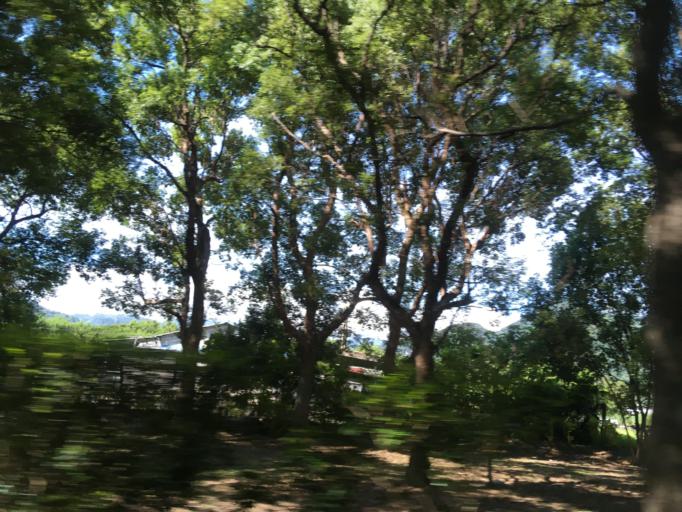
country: TW
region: Taiwan
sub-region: Yilan
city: Yilan
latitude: 24.4672
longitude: 121.7938
